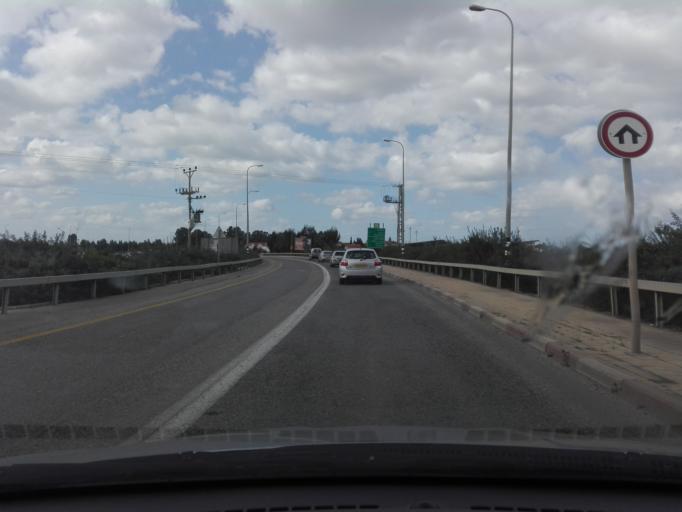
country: IL
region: Haifa
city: Qesarya
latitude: 32.5112
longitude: 34.9561
